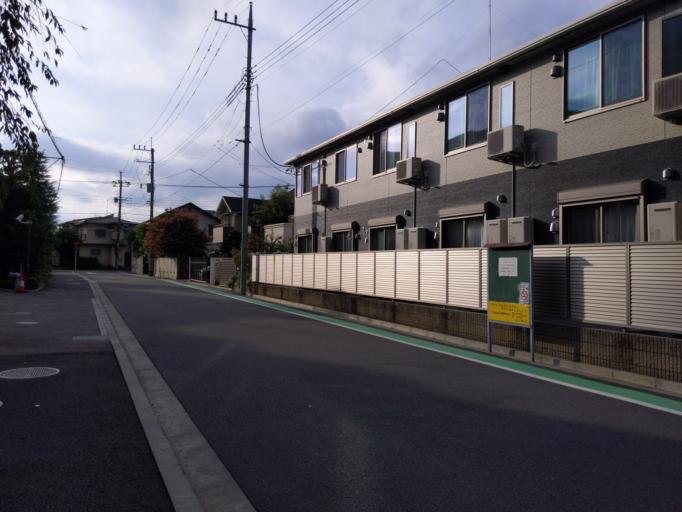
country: JP
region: Tokyo
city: Chofugaoka
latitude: 35.6393
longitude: 139.5845
